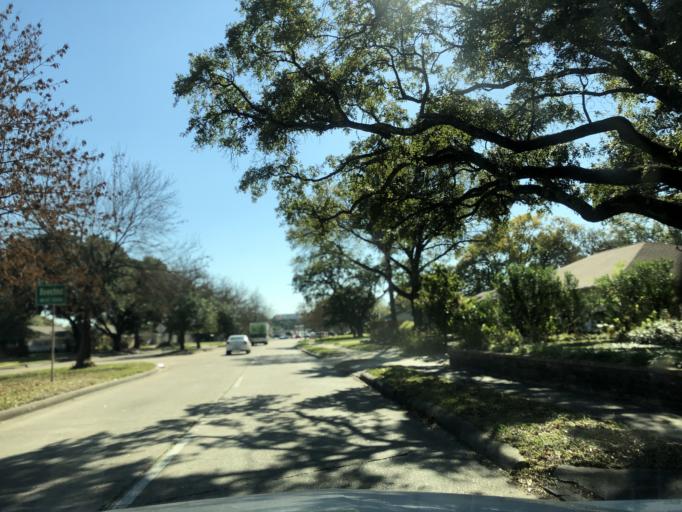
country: US
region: Texas
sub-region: Harris County
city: Bellaire
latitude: 29.6902
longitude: -95.4929
